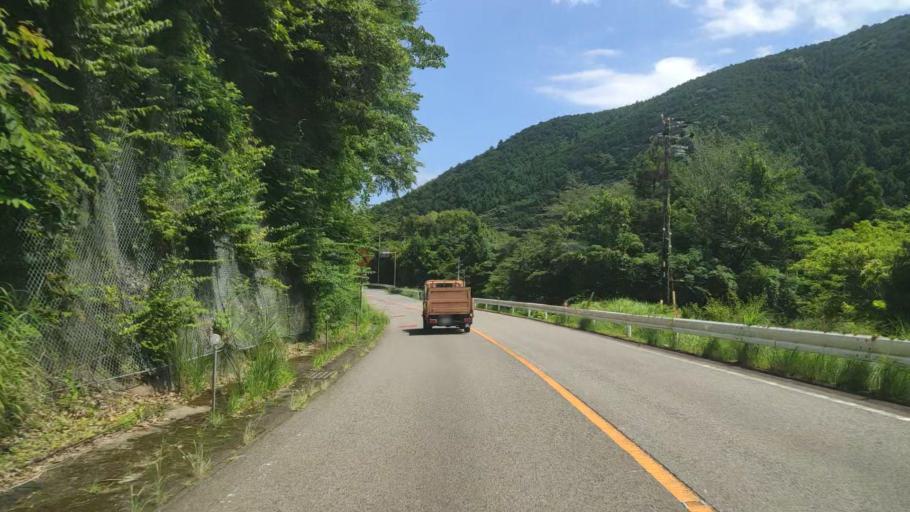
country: JP
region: Mie
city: Owase
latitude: 33.9189
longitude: 136.1074
